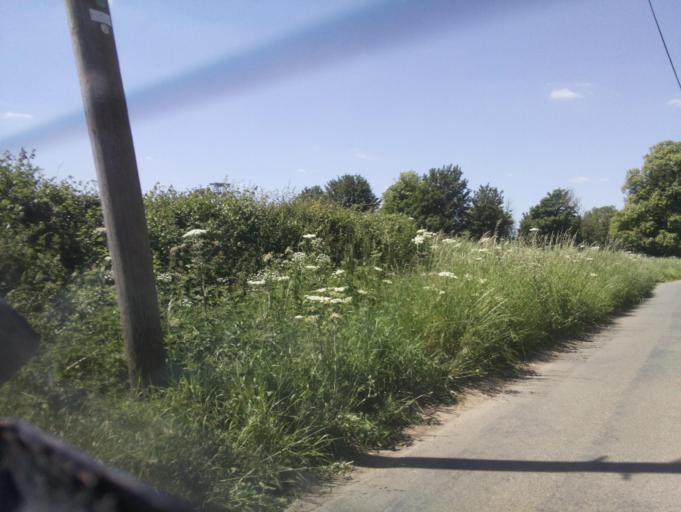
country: GB
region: England
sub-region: Wiltshire
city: Bremhill
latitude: 51.4671
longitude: -2.0760
